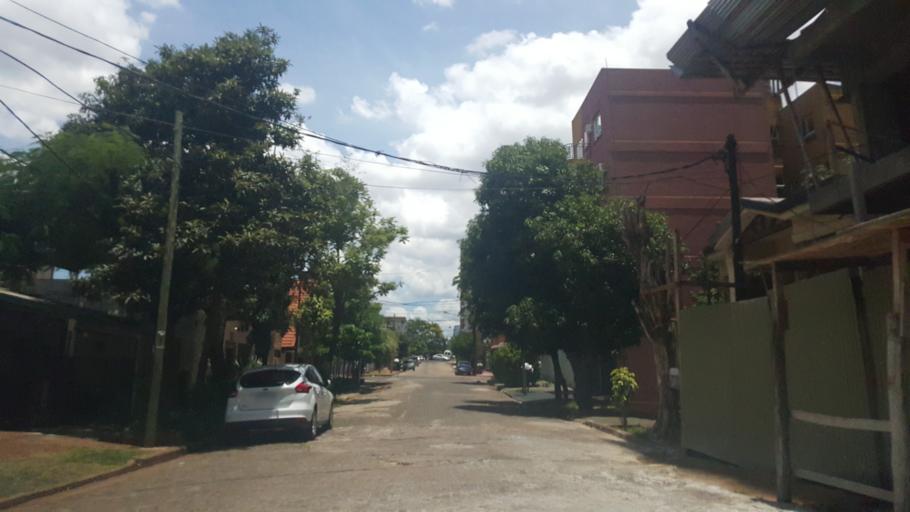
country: AR
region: Misiones
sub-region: Departamento de Capital
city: Posadas
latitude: -27.3643
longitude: -55.9037
